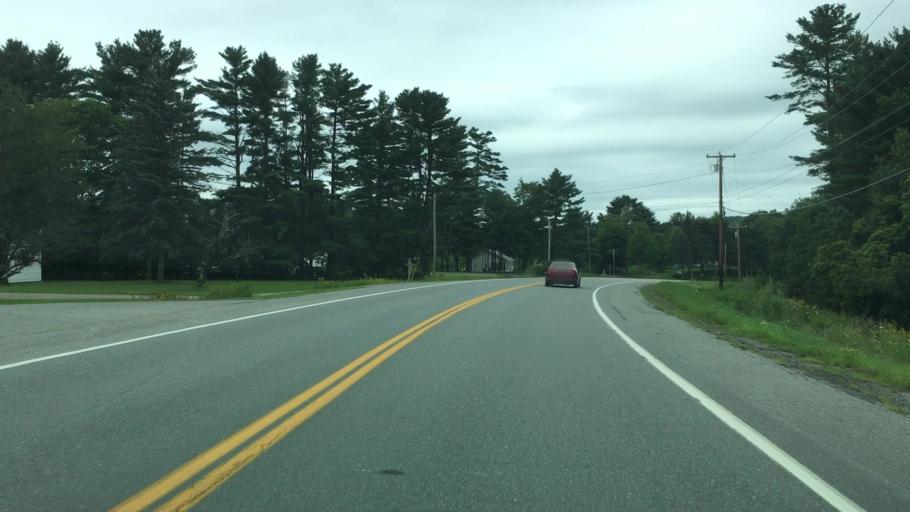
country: US
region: Maine
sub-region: Waldo County
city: Frankfort
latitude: 44.6201
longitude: -68.8703
